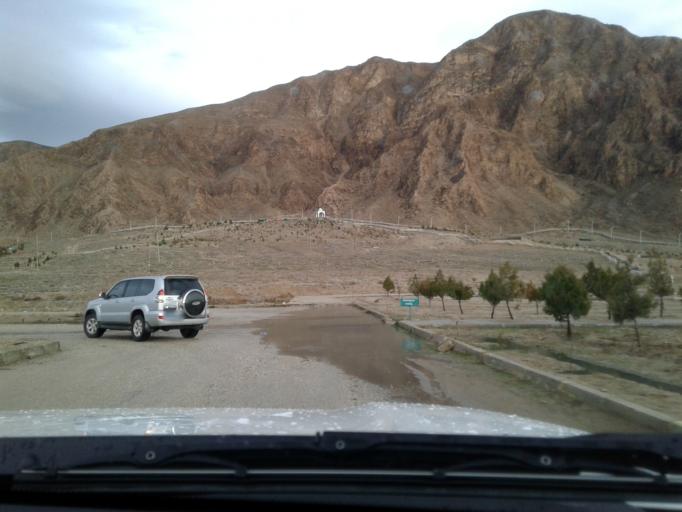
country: TM
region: Balkan
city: Balkanabat
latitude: 39.5380
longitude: 54.3510
